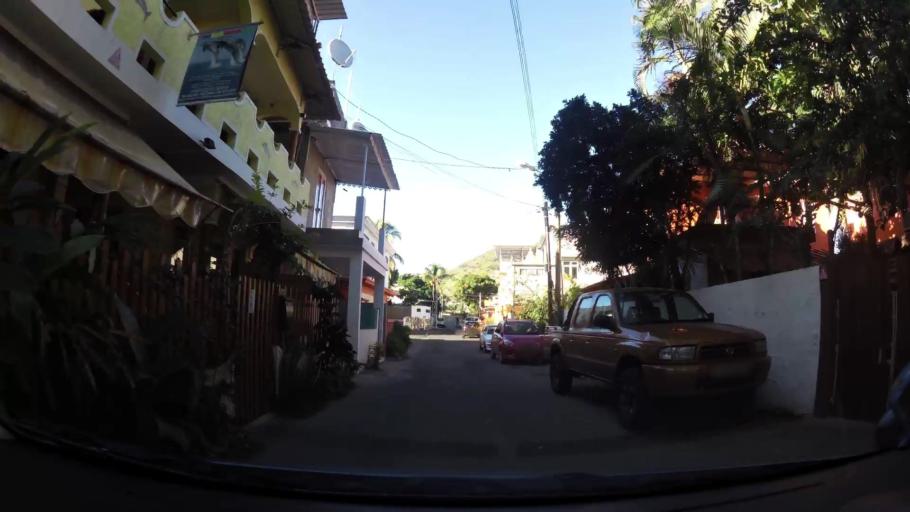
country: MU
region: Black River
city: Tamarin
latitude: -20.3280
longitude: 57.3774
